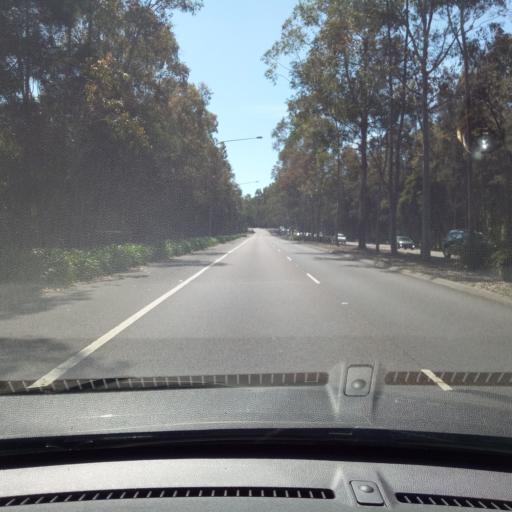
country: AU
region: New South Wales
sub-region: Wyong Shire
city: Chittaway Bay
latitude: -33.3385
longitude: 151.4292
